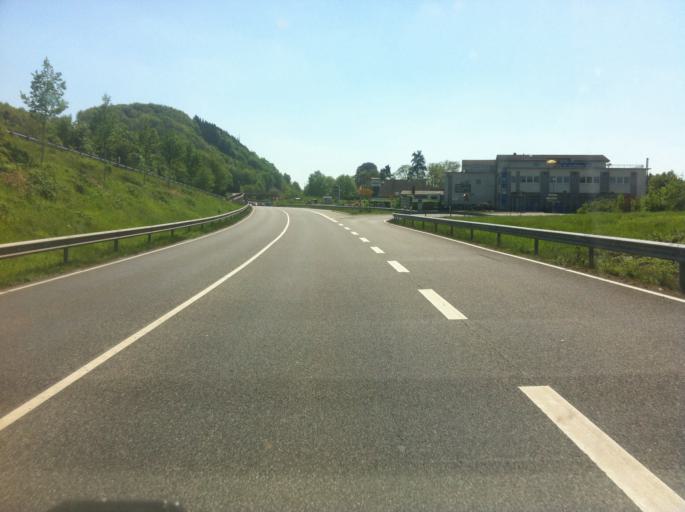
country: DE
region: Rheinland-Pfalz
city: Unkel
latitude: 50.6072
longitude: 7.2197
